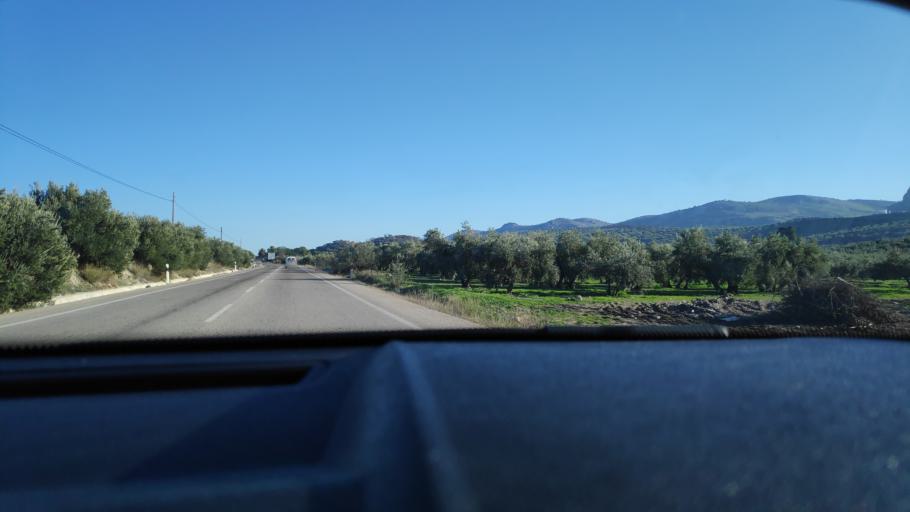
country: ES
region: Andalusia
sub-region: Province of Cordoba
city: Luque
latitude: 37.5795
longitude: -4.2799
